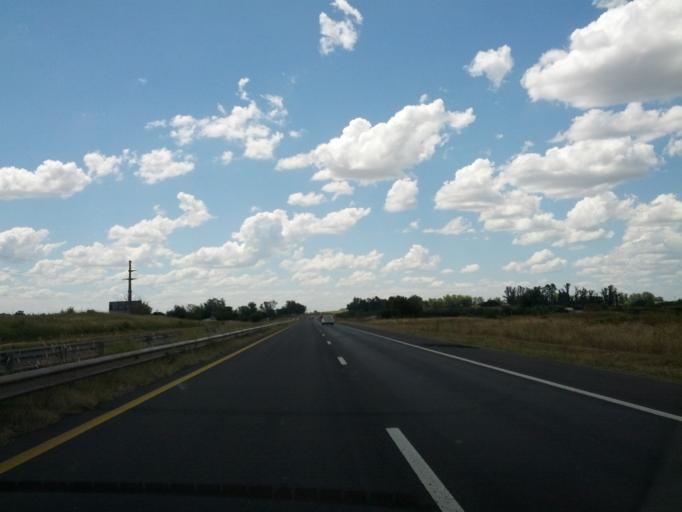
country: AR
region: Entre Rios
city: Concepcion del Uruguay
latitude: -32.3984
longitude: -58.2785
